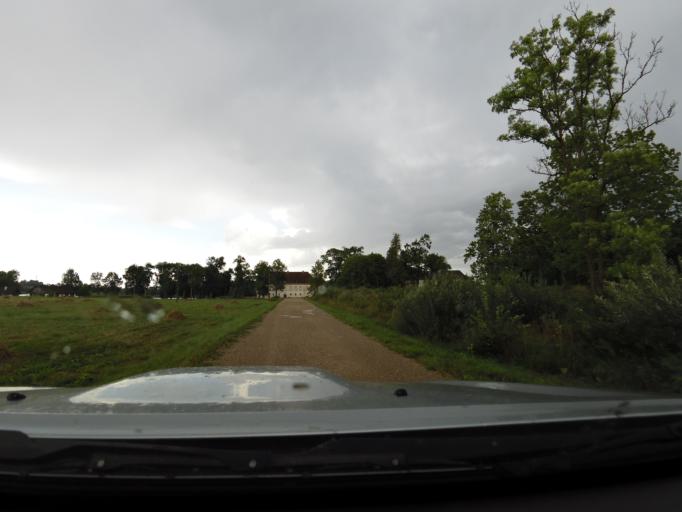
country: LT
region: Vilnius County
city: Ukmerge
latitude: 55.2844
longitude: 24.5127
